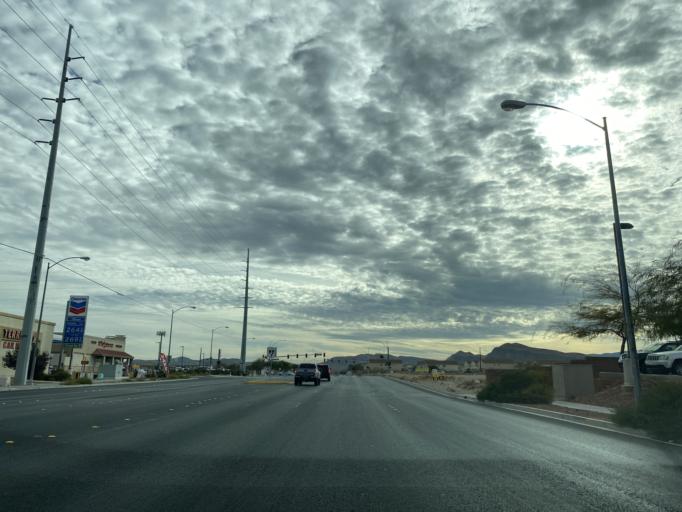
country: US
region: Nevada
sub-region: Clark County
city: Enterprise
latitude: 36.0222
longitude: -115.2791
